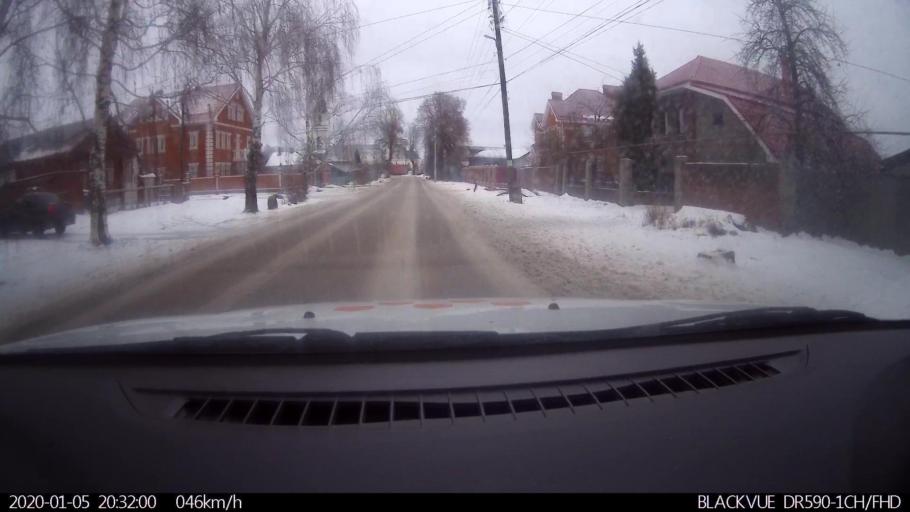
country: RU
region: Nizjnij Novgorod
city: Lukino
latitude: 56.4100
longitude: 43.7290
